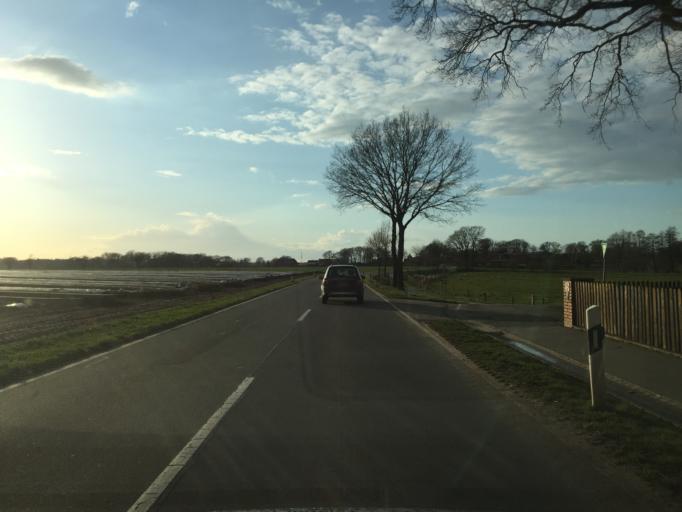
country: DE
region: Lower Saxony
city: Steyerberg
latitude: 52.5663
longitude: 9.0039
